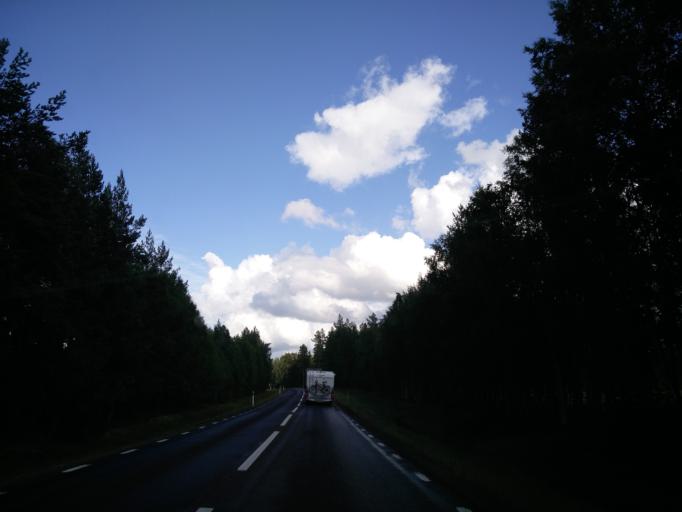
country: SE
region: Vaermland
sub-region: Hagfors Kommun
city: Ekshaerad
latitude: 60.4781
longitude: 13.3655
